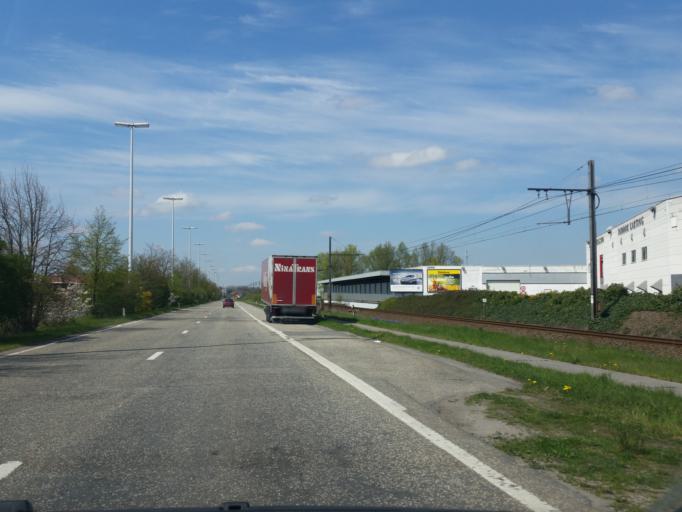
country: BE
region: Flanders
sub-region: Provincie Oost-Vlaanderen
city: Sint-Niklaas
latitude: 51.1661
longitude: 4.1662
